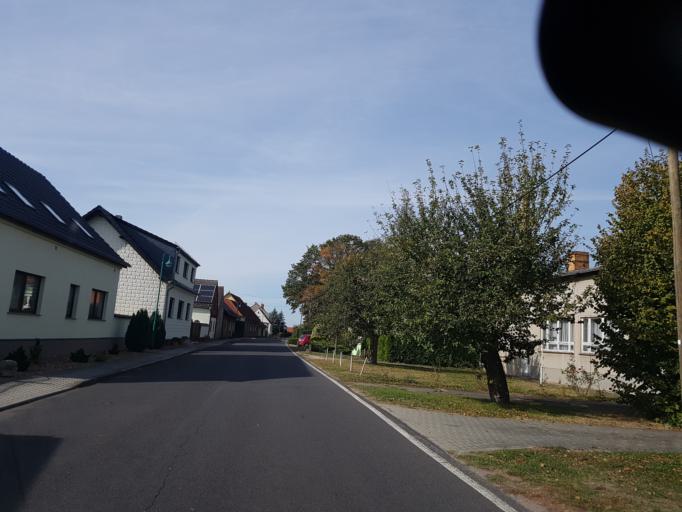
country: DE
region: Brandenburg
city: Schlieben
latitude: 51.7778
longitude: 13.3191
